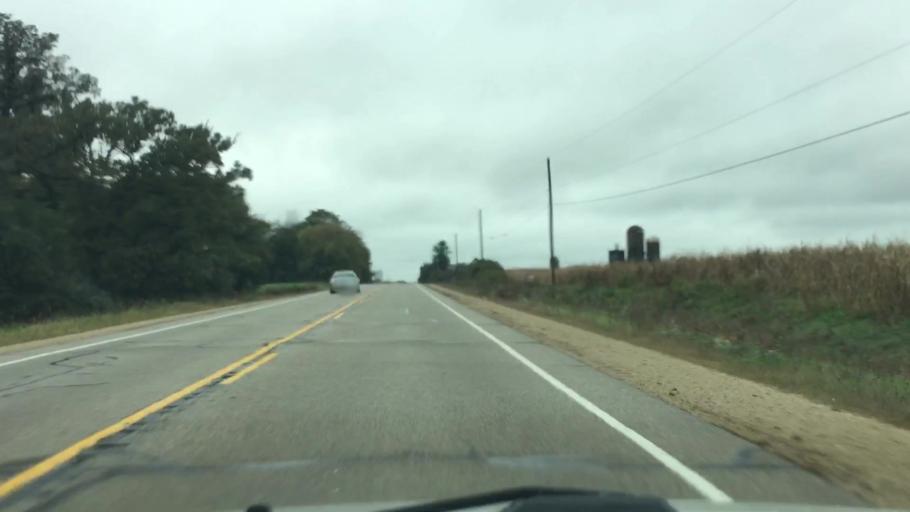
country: US
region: Wisconsin
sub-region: Rock County
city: Milton
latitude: 42.7720
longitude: -88.8910
